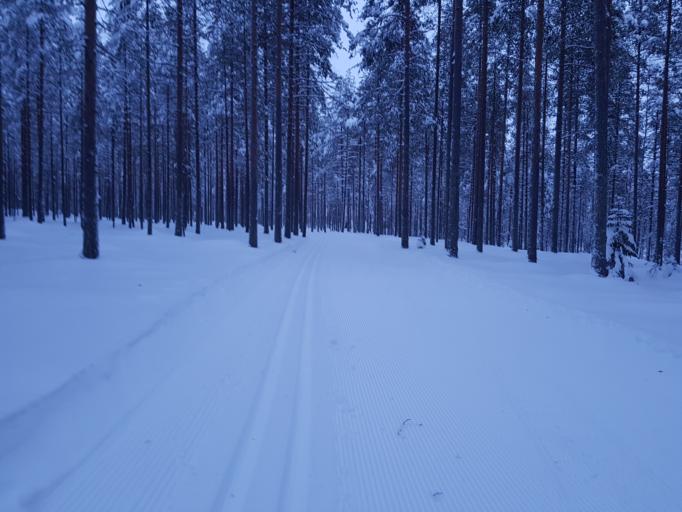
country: FI
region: Kainuu
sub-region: Kehys-Kainuu
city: Kuhmo
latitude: 64.0843
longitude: 29.5209
